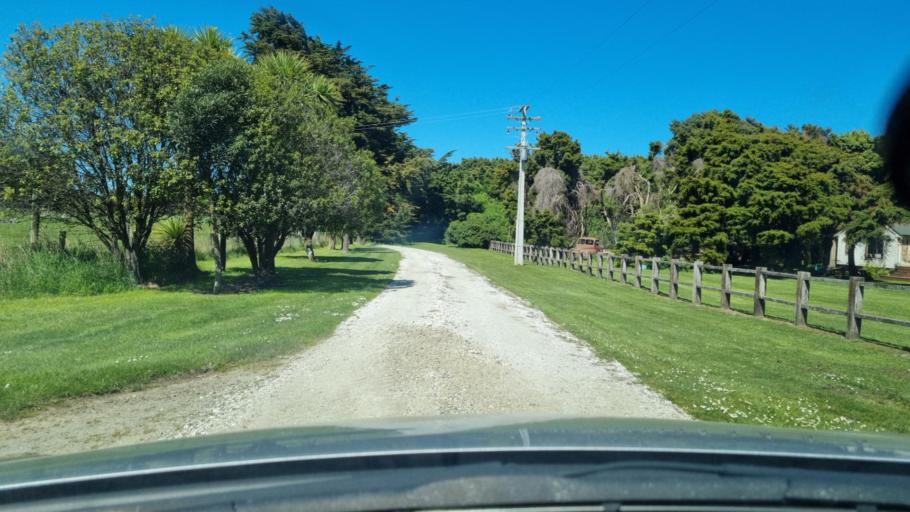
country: NZ
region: Southland
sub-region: Invercargill City
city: Invercargill
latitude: -46.4568
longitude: 168.2813
